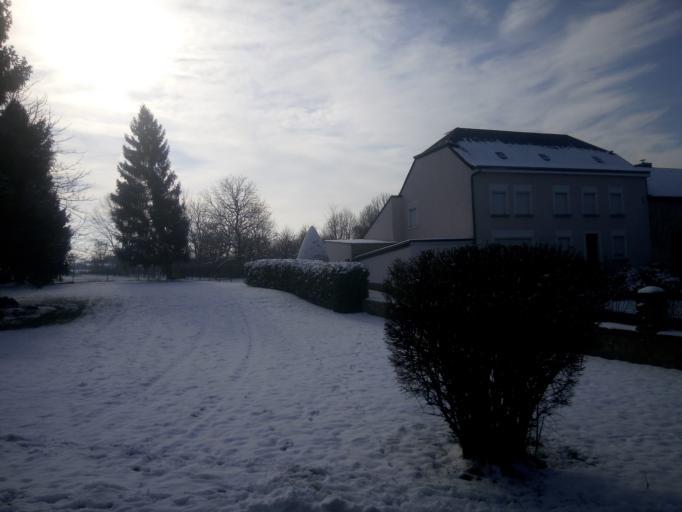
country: LU
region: Grevenmacher
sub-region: Canton d'Echternach
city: Consdorf
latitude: 49.7806
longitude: 6.3418
